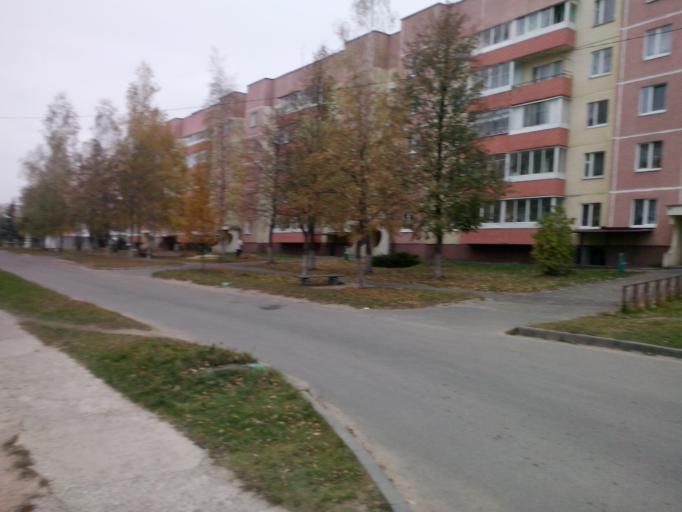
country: BY
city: Novolukoml'
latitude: 54.6494
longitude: 29.1379
